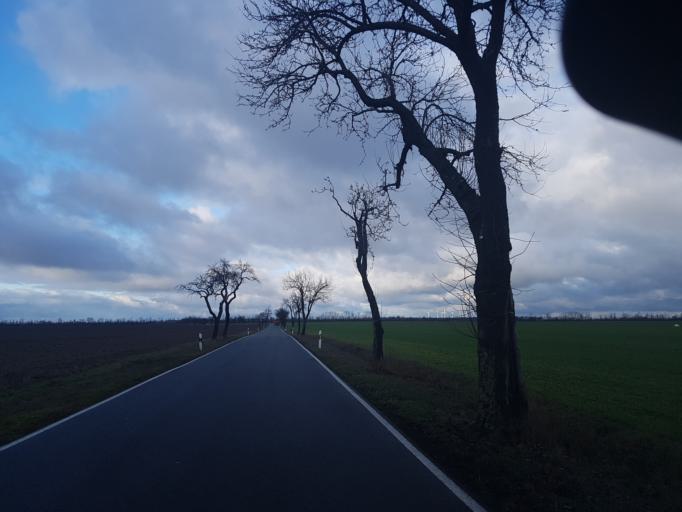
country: DE
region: Brandenburg
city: Muhlberg
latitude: 51.4077
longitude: 13.2406
